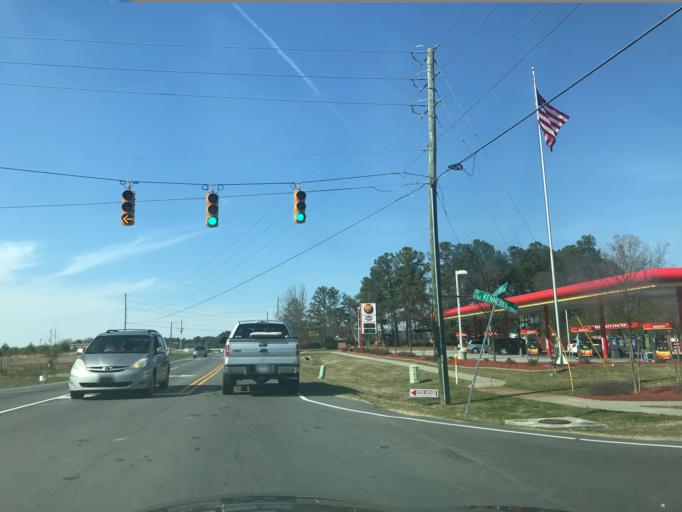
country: US
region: North Carolina
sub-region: Harnett County
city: Angier
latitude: 35.5369
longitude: -78.7466
